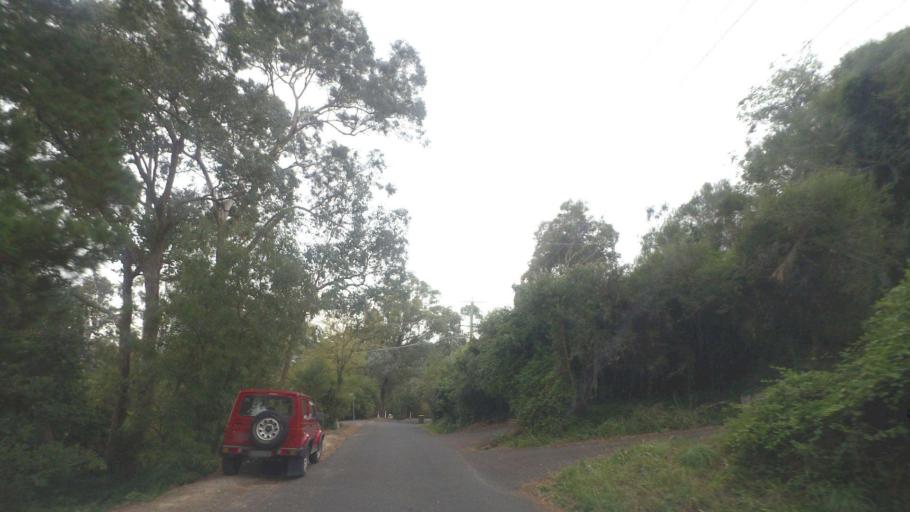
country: AU
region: Victoria
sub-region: Nillumbik
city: North Warrandyte
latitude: -37.7480
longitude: 145.2020
